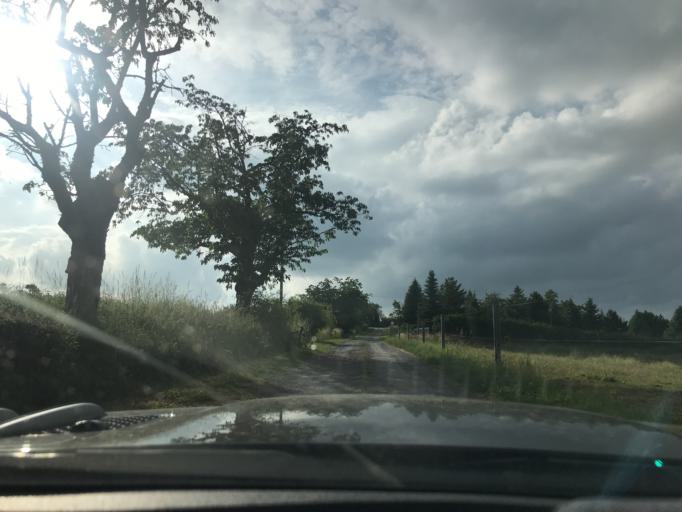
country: DE
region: Thuringia
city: Muehlhausen
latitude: 51.2108
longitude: 10.4169
